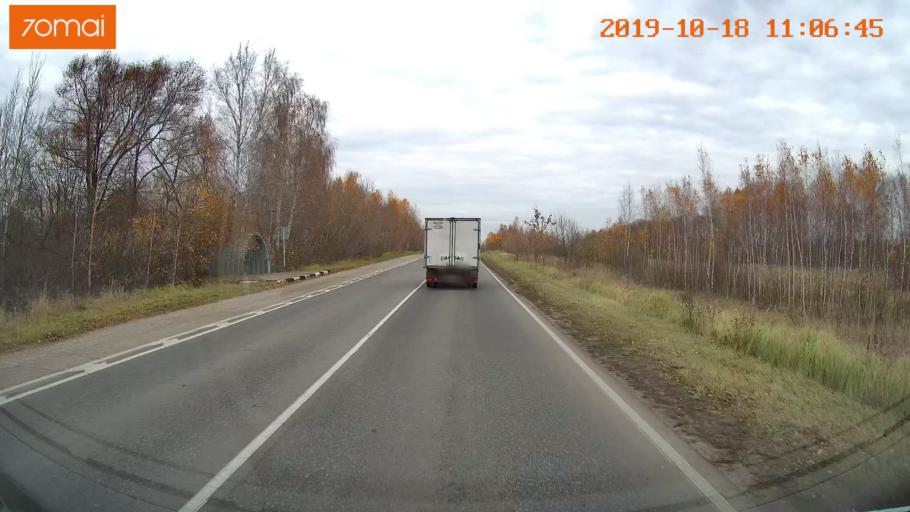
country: RU
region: Tula
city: Kimovsk
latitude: 53.9210
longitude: 38.5348
